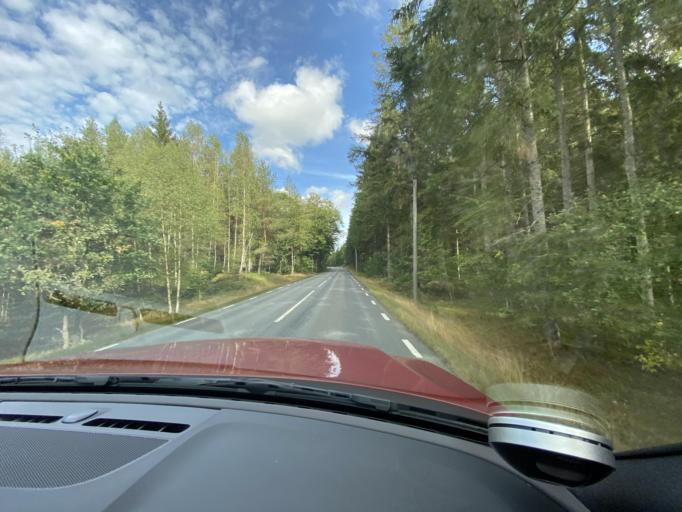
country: SE
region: Skane
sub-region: Hassleholms Kommun
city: Bjarnum
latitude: 56.3385
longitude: 13.6879
